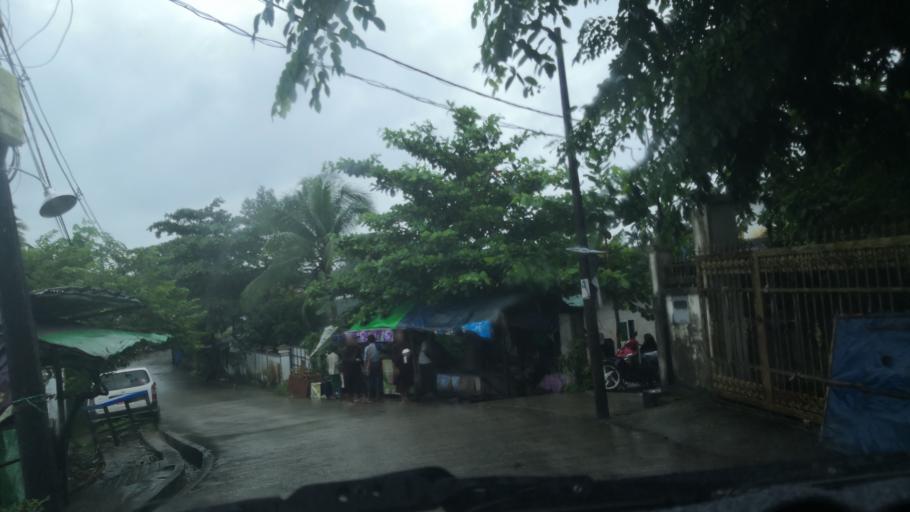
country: MM
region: Yangon
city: Yangon
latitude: 16.8802
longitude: 96.1485
